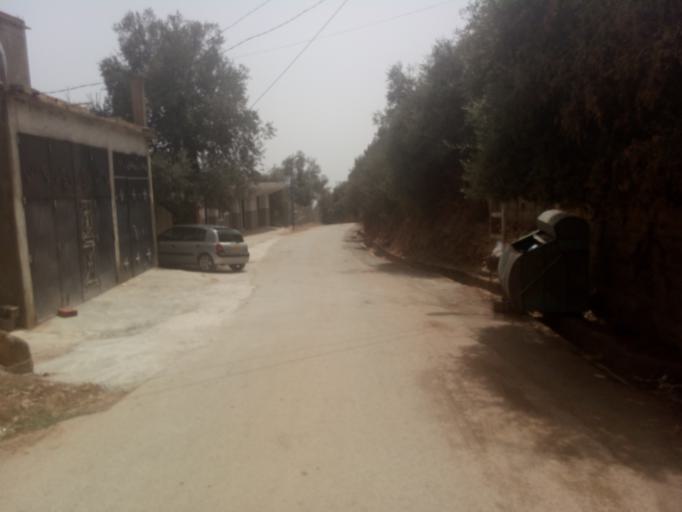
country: DZ
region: Tizi Ouzou
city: Chemini
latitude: 36.6044
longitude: 4.6386
